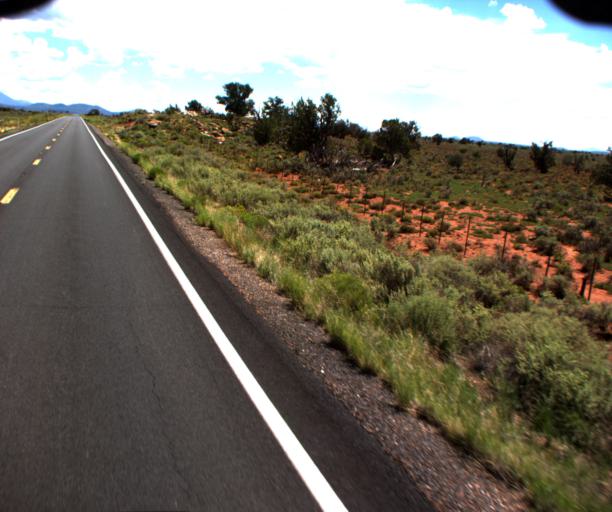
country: US
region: Arizona
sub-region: Coconino County
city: Williams
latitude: 35.6401
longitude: -112.1266
